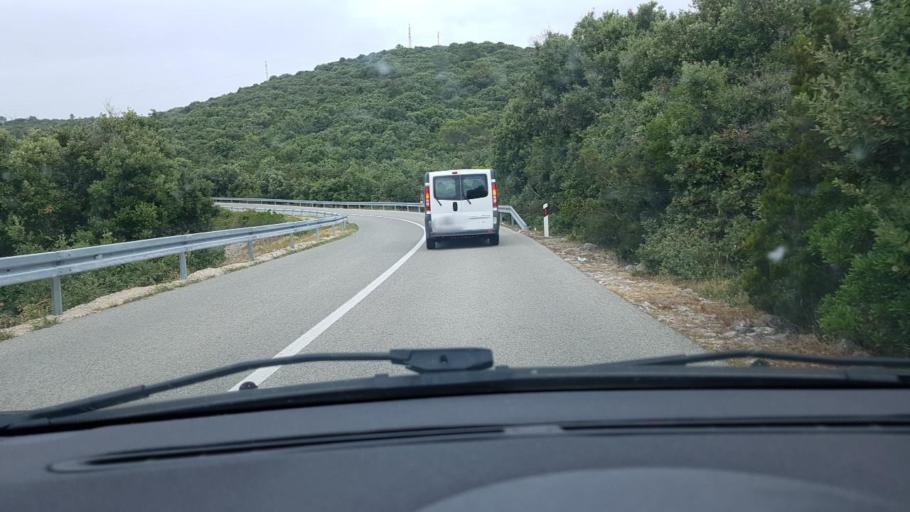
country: HR
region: Dubrovacko-Neretvanska
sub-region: Grad Korcula
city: Zrnovo
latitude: 42.9426
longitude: 17.0074
